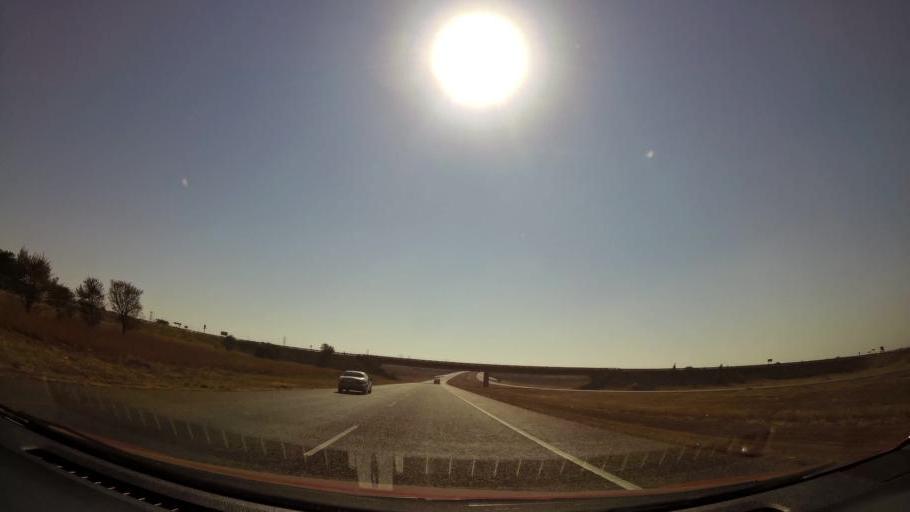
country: ZA
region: Gauteng
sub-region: City of Tshwane Metropolitan Municipality
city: Mabopane
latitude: -25.5584
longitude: 28.1079
